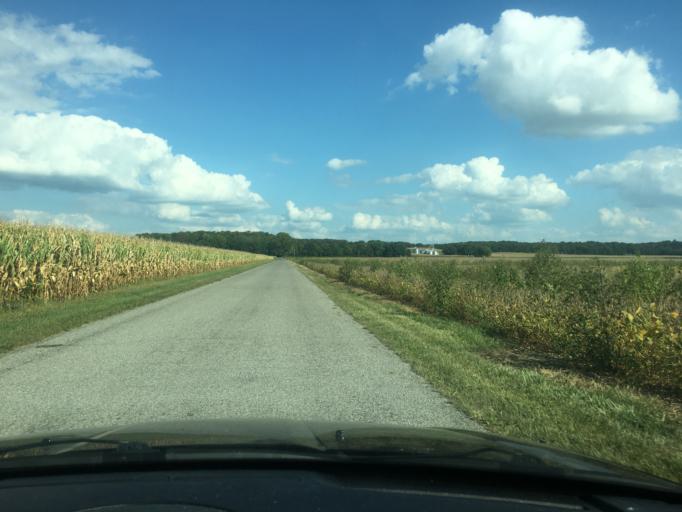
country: US
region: Ohio
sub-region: Logan County
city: West Liberty
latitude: 40.2451
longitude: -83.7364
